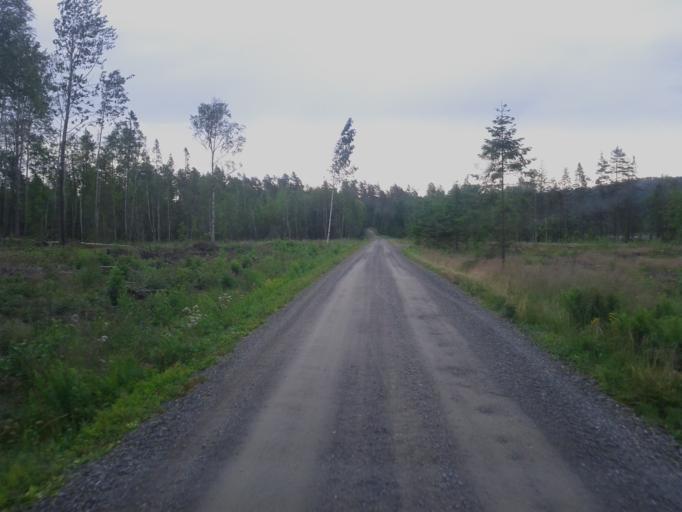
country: SE
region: Vaesternorrland
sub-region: OErnskoeldsviks Kommun
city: Bjasta
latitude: 63.0824
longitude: 18.4683
